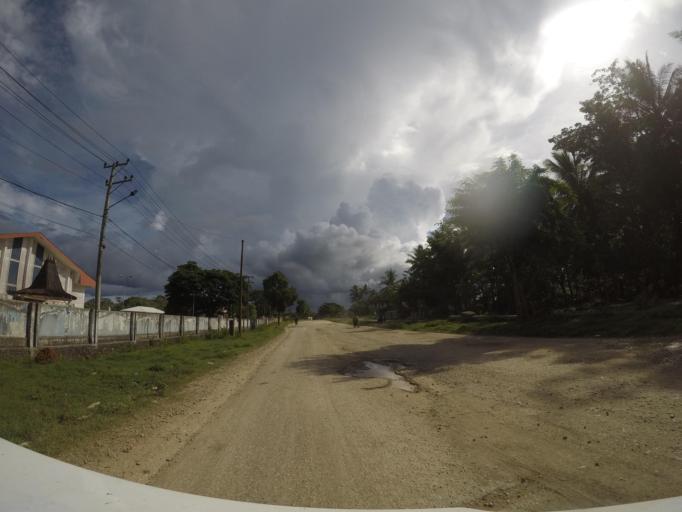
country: TL
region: Lautem
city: Lospalos
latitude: -8.4924
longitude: 126.9927
